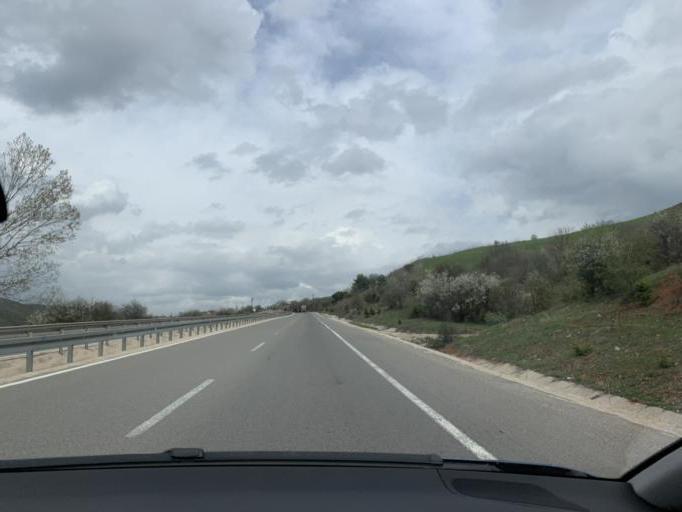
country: TR
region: Bolu
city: Gerede
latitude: 40.7869
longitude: 32.1186
